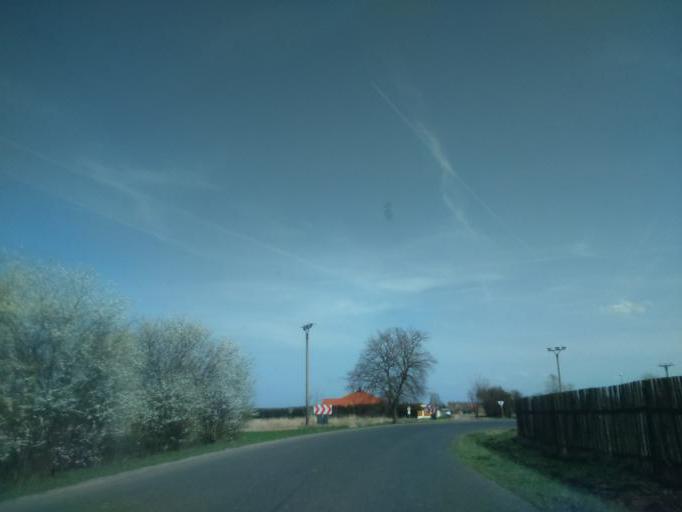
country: CZ
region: Plzensky
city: Hermanova Hut'
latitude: 49.7049
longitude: 13.1244
